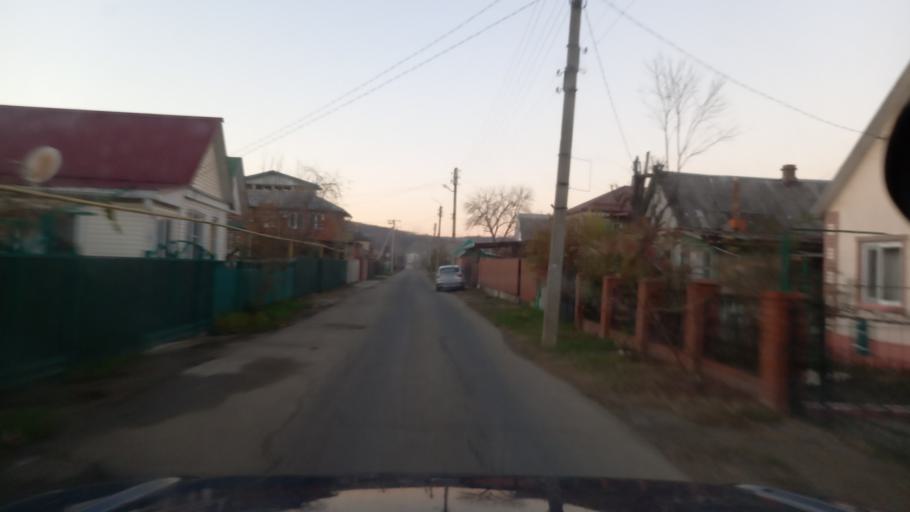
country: RU
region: Krasnodarskiy
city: Goryachiy Klyuch
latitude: 44.6290
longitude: 39.1044
